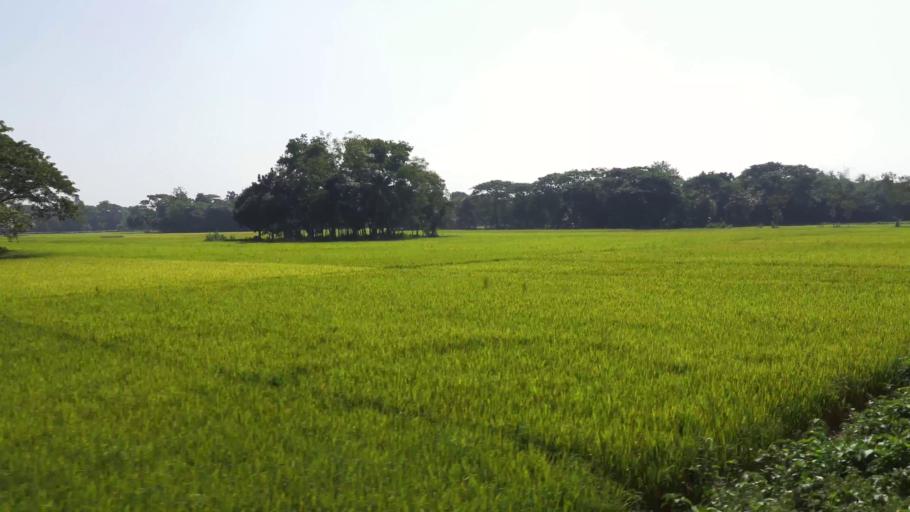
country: BD
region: Dhaka
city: Gafargaon
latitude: 24.5063
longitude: 90.5172
